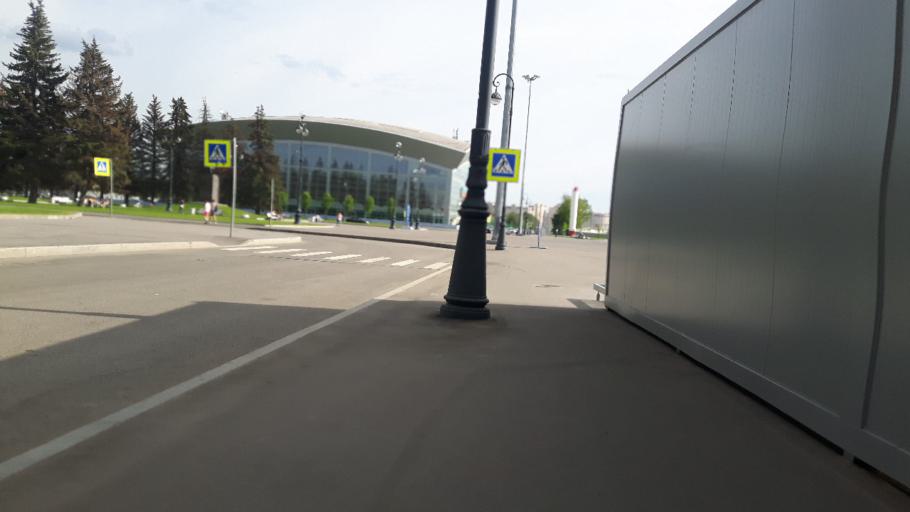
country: RU
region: St.-Petersburg
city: Staraya Derevnya
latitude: 59.9737
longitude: 30.2259
